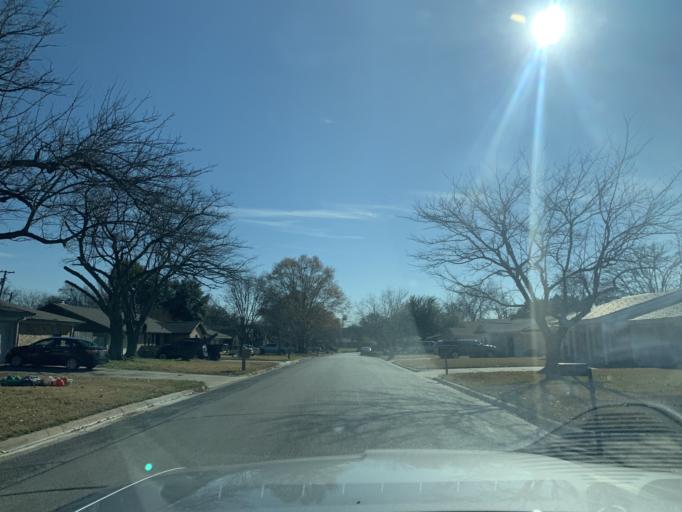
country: US
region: Texas
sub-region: Tarrant County
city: Bedford
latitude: 32.8431
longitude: -97.1510
